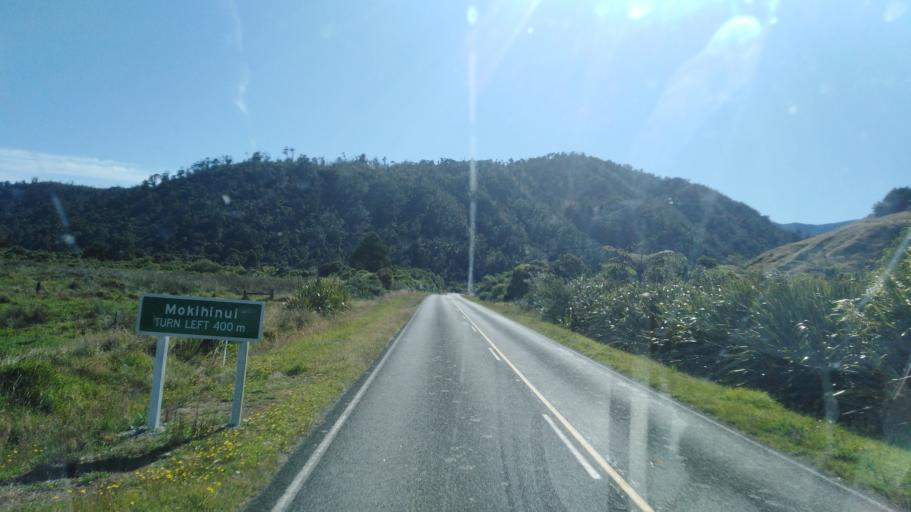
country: NZ
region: West Coast
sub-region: Buller District
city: Westport
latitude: -41.5313
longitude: 171.9406
